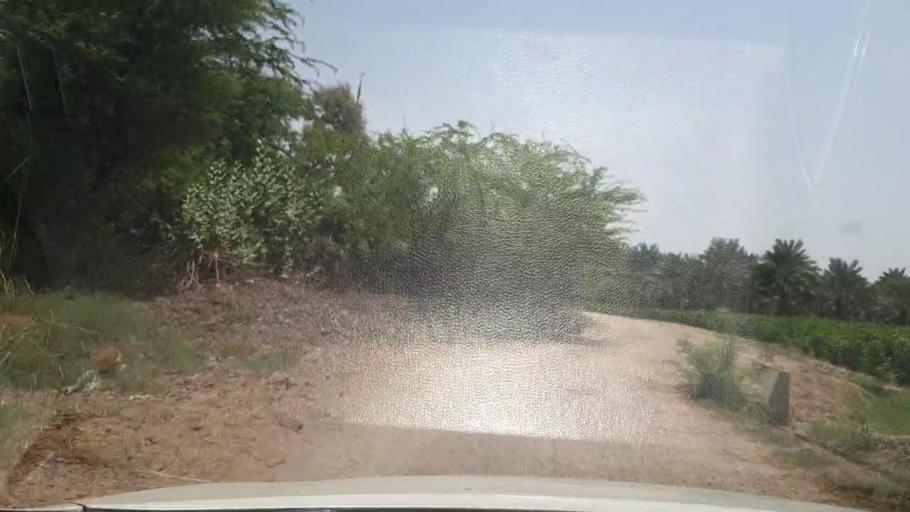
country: PK
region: Sindh
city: Bozdar
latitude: 27.2177
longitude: 68.6560
